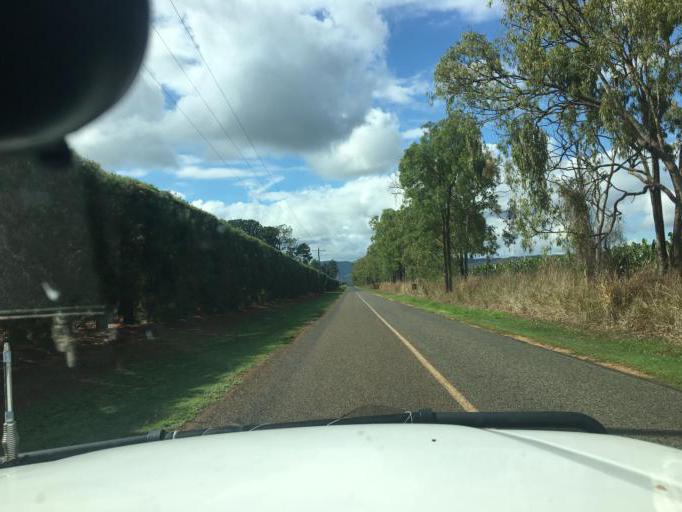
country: AU
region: Queensland
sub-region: Tablelands
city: Mareeba
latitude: -17.1086
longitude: 145.4109
